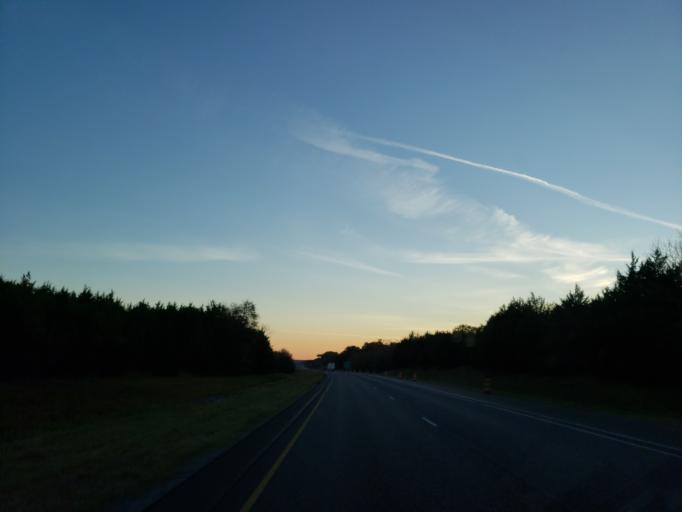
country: US
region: Alabama
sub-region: Sumter County
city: Livingston
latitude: 32.6456
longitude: -88.1965
